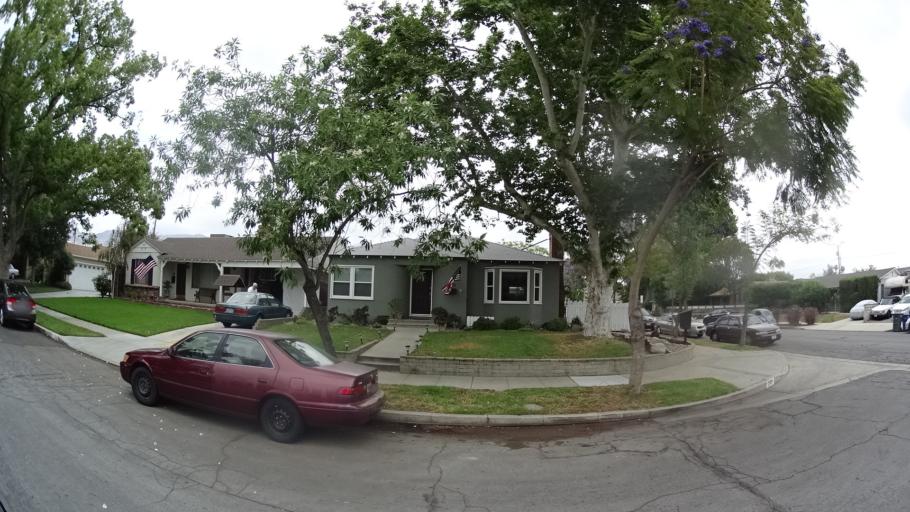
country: US
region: California
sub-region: Los Angeles County
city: Burbank
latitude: 34.1748
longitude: -118.3208
